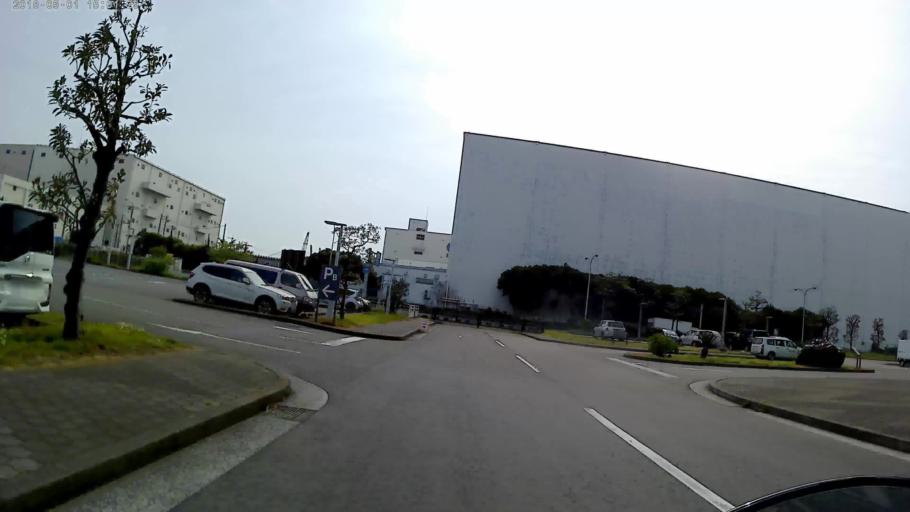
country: JP
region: Kanagawa
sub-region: Kawasaki-shi
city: Kawasaki
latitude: 35.4961
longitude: 139.7633
